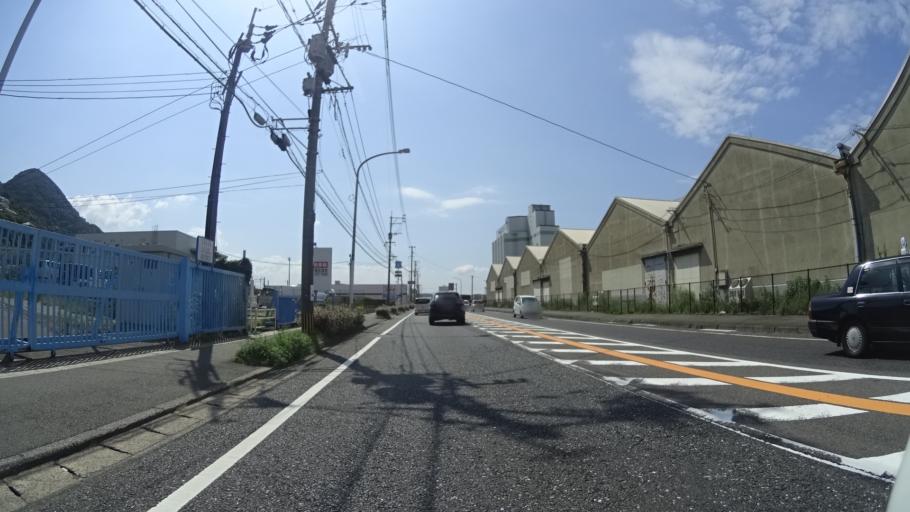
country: JP
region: Yamaguchi
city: Shimonoseki
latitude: 33.9400
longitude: 130.9521
